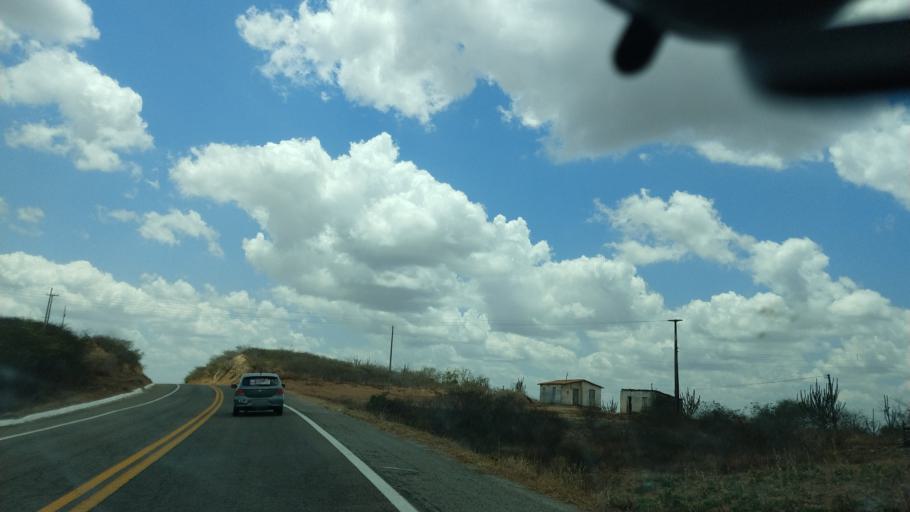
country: BR
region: Rio Grande do Norte
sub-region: Cerro Cora
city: Cerro Cora
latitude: -6.1878
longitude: -36.2366
